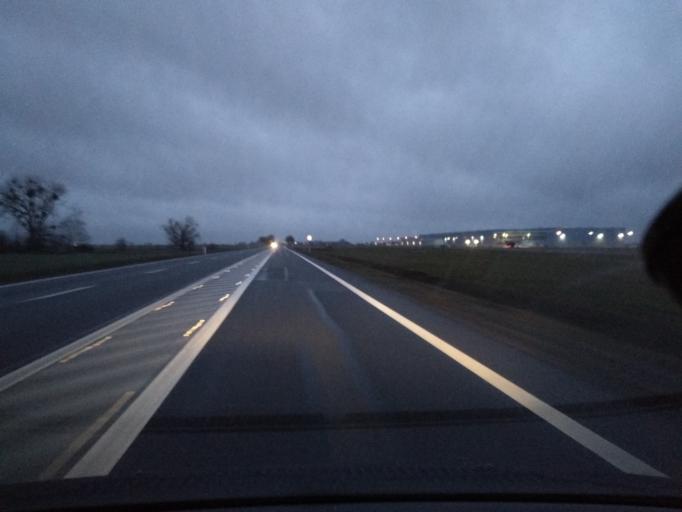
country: PL
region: Lower Silesian Voivodeship
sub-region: Powiat sredzki
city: Szczepanow
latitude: 51.1638
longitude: 16.6590
